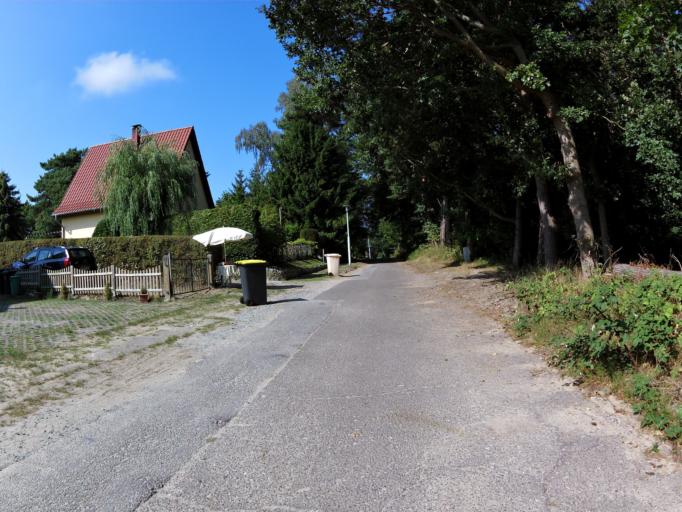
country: DE
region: Mecklenburg-Vorpommern
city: Loddin
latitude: 54.0191
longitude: 14.0484
